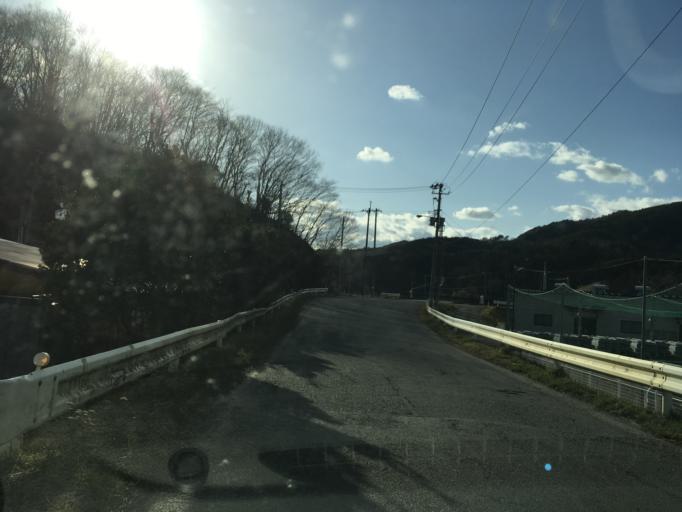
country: JP
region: Iwate
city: Ofunato
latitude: 39.0307
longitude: 141.6046
